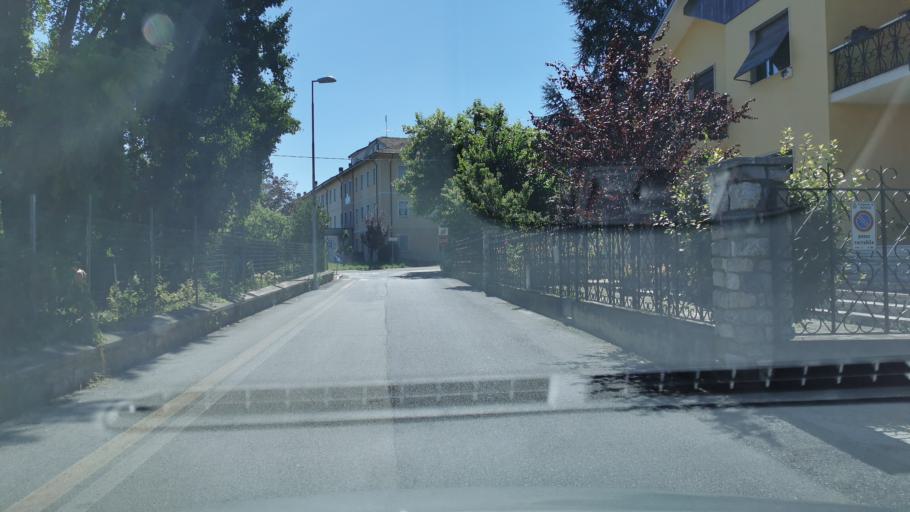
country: IT
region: Piedmont
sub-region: Provincia di Cuneo
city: Boves
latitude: 44.3278
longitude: 7.5545
